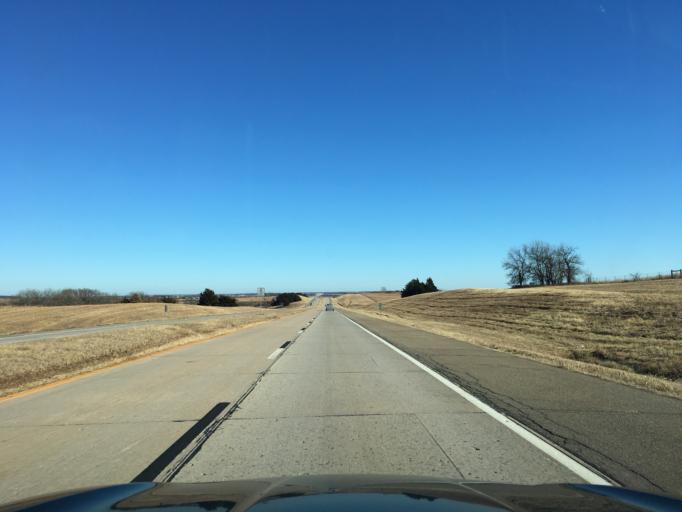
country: US
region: Oklahoma
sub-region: Payne County
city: Yale
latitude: 36.2240
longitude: -96.7427
